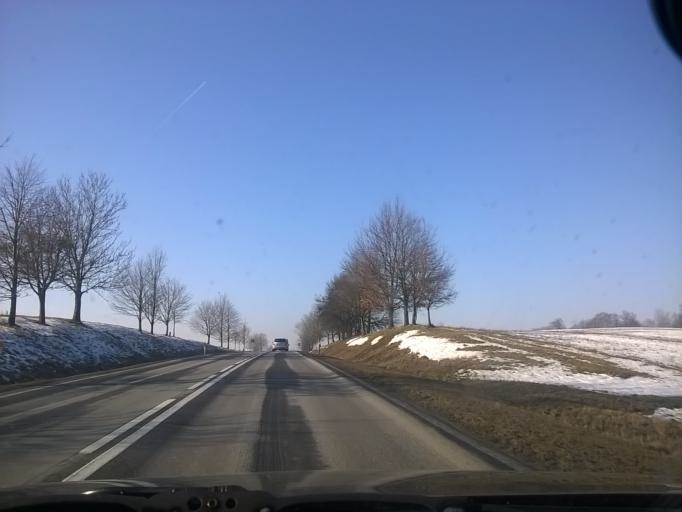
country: PL
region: Warmian-Masurian Voivodeship
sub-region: Powiat mragowski
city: Mragowo
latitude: 53.8420
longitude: 21.1639
